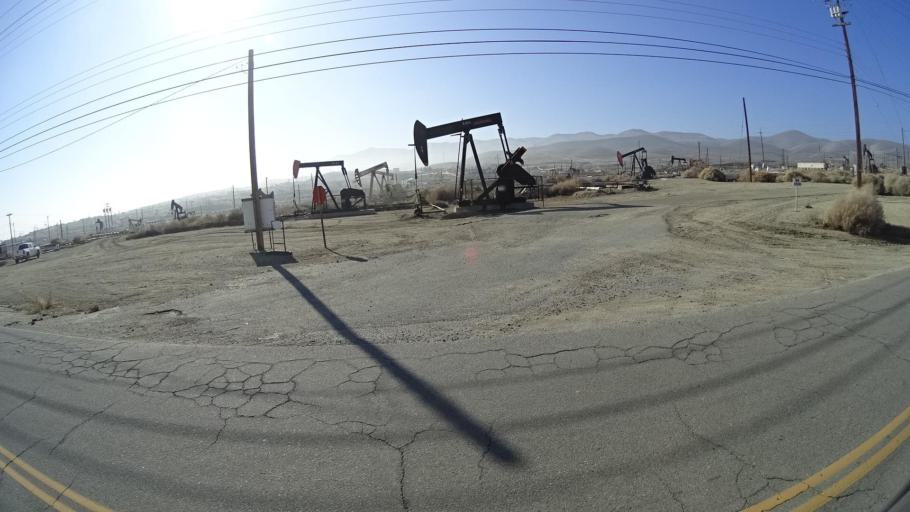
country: US
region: California
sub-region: Kern County
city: Taft Heights
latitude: 35.2233
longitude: -119.6205
